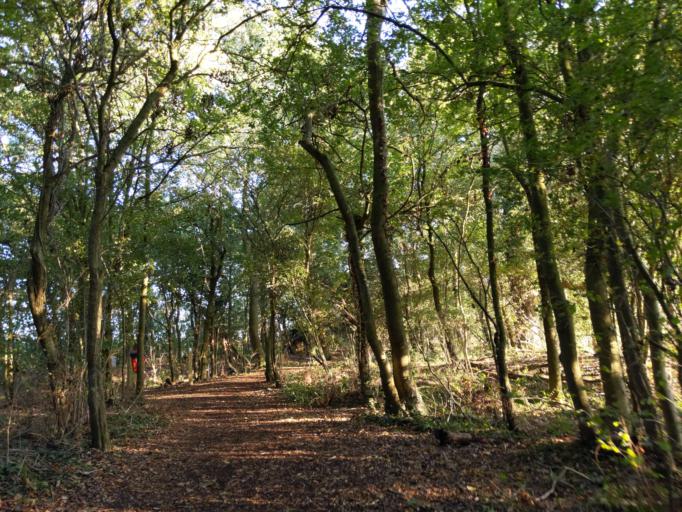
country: GB
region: England
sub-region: Oxfordshire
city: Radley
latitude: 51.6987
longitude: -1.2477
